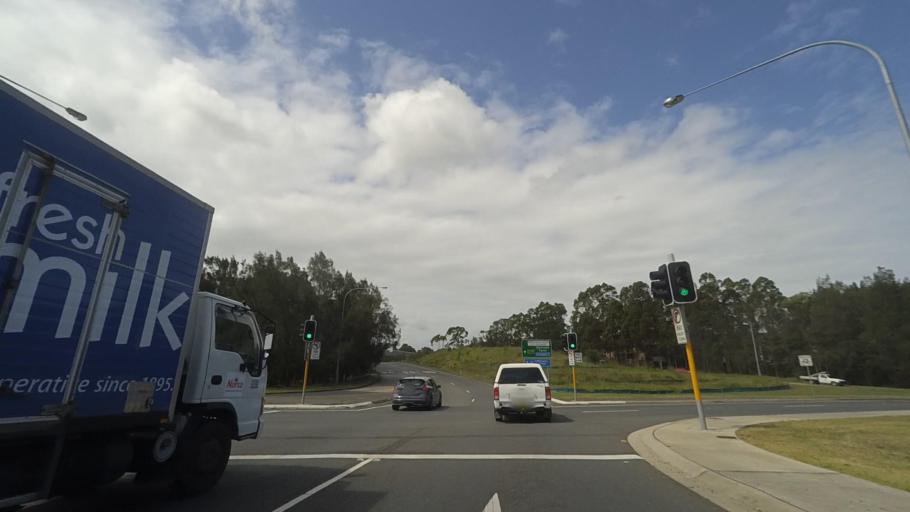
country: AU
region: New South Wales
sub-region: Newcastle
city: Lambton
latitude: -32.9058
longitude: 151.6922
